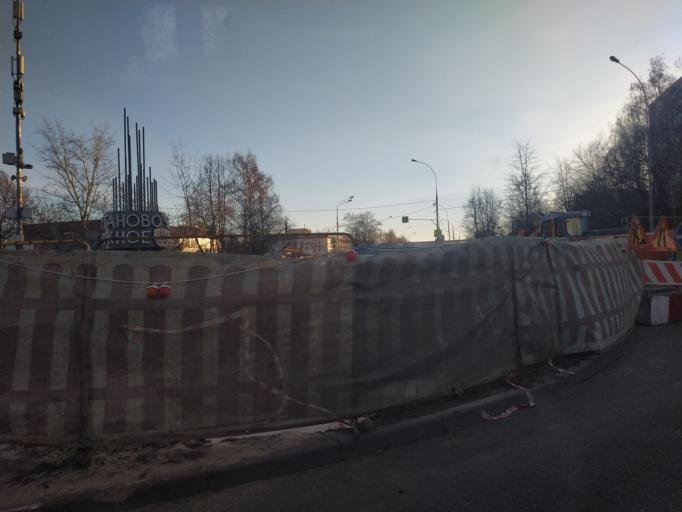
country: RU
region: Moskovskaya
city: Biryulevo Zapadnoye
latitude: 55.6008
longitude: 37.6214
